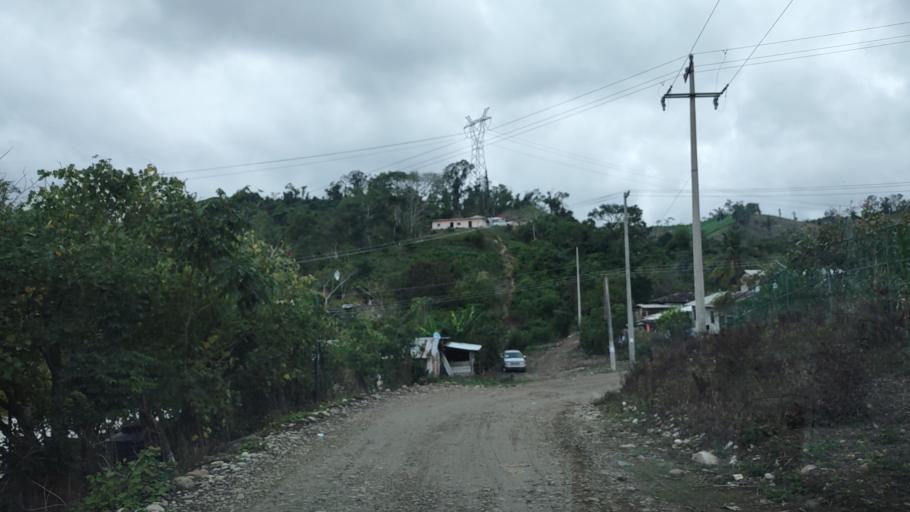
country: MX
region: Veracruz
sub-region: Coatzintla
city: Manuel Maria Contreras
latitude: 20.4067
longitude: -97.4561
